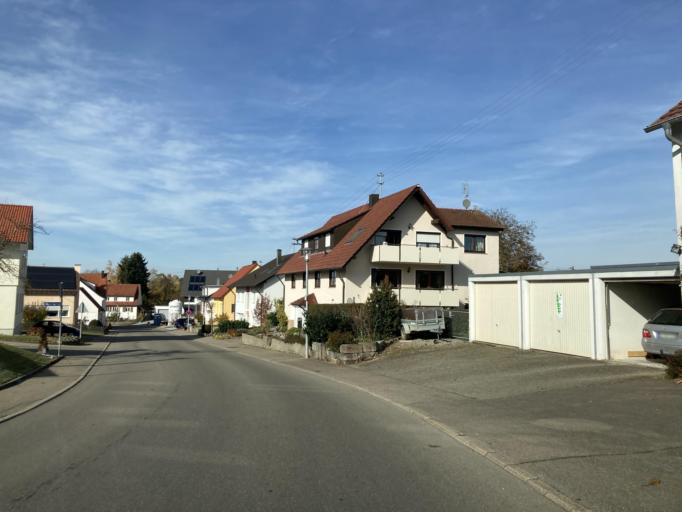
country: DE
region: Baden-Wuerttemberg
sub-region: Tuebingen Region
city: Bodelshausen
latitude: 48.3815
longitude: 8.9725
